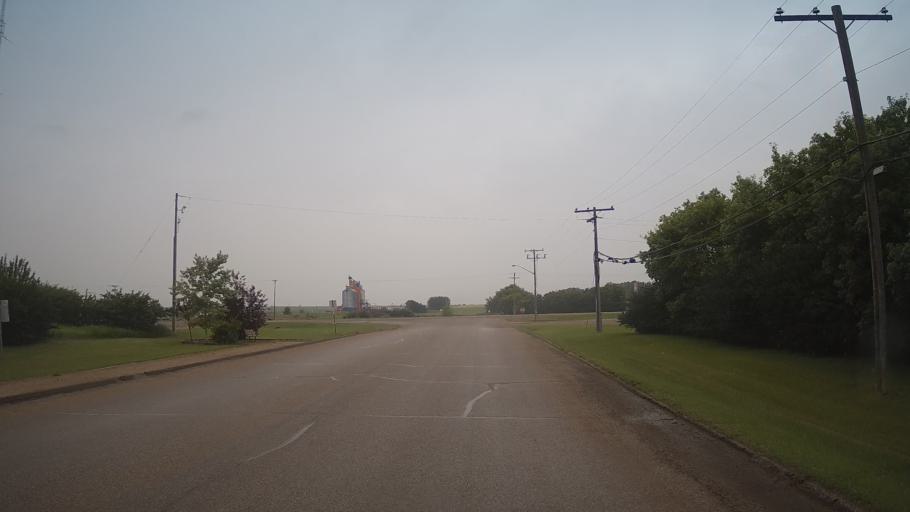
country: CA
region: Saskatchewan
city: Biggar
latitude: 52.0574
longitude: -107.9987
